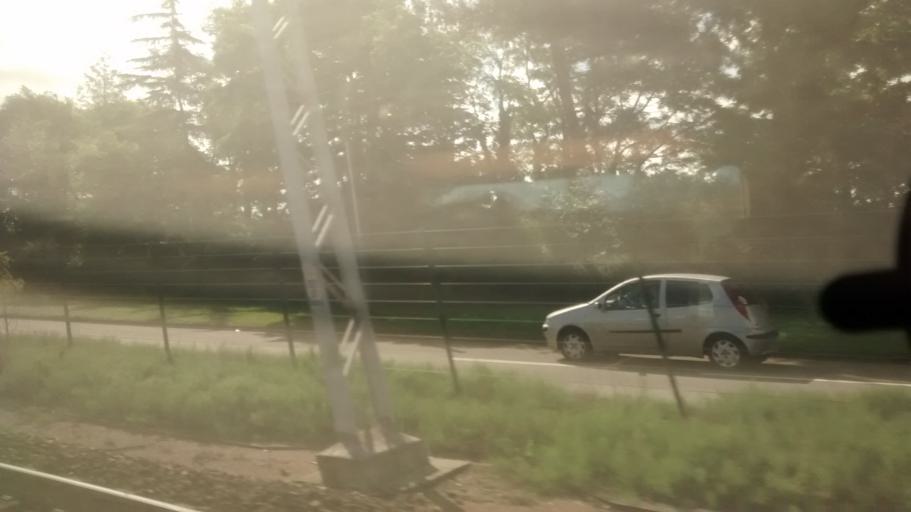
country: FR
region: Pays de la Loire
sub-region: Departement de la Sarthe
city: Sarge-les-le-Mans
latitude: 47.9994
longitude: 0.2398
